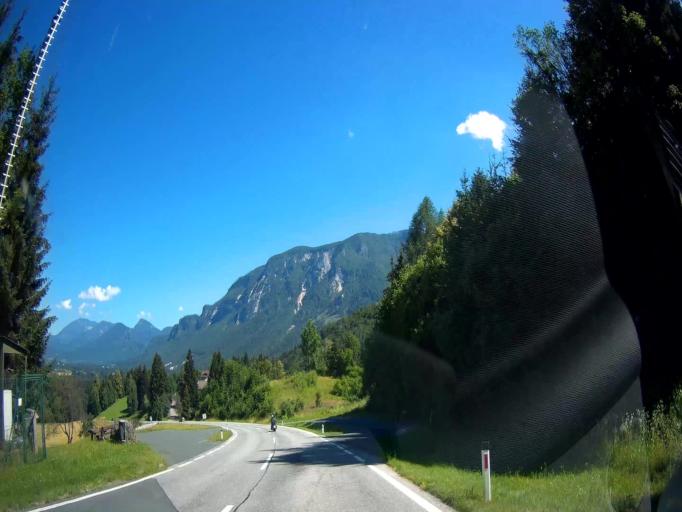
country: AT
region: Carinthia
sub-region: Politischer Bezirk Volkermarkt
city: Gallizien
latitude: 46.5537
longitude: 14.4909
